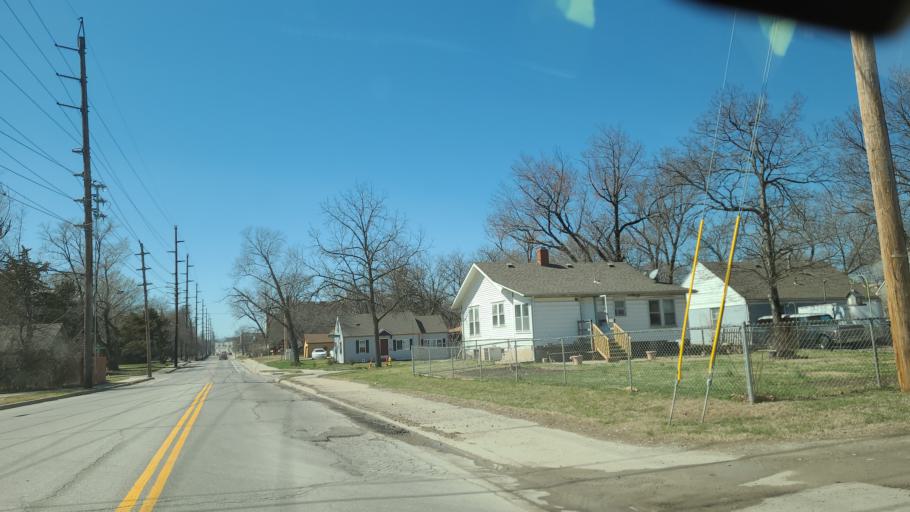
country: US
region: Kansas
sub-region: Douglas County
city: Lawrence
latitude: 38.9501
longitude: -95.2459
